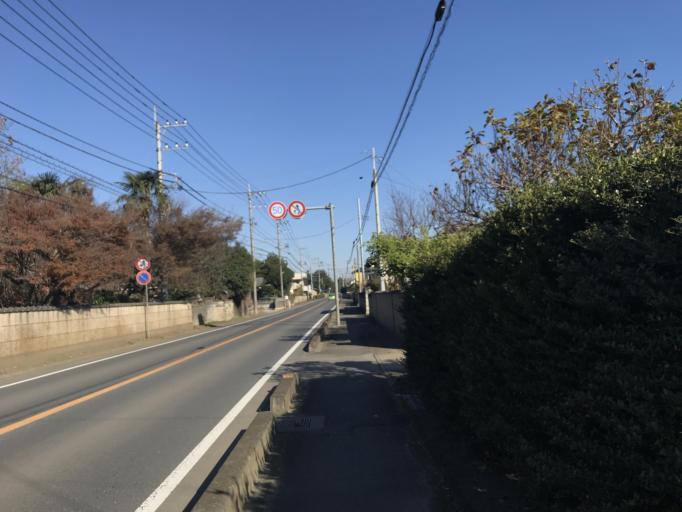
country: JP
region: Ibaraki
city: Yuki
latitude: 36.2677
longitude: 139.8434
